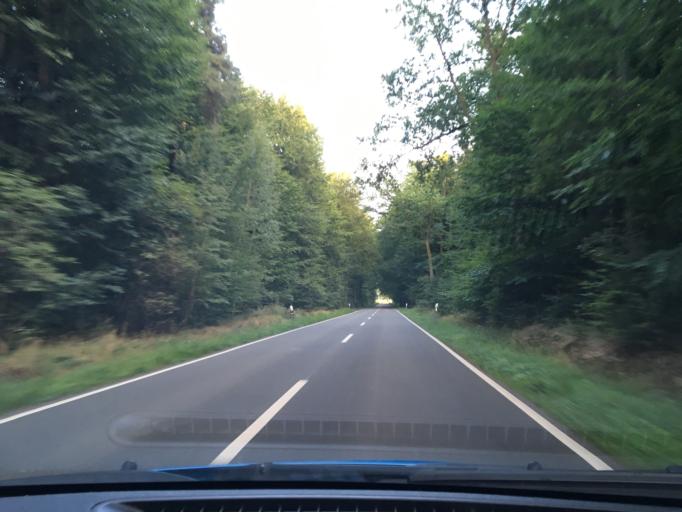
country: DE
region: Lower Saxony
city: Tosterglope
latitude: 53.2258
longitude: 10.8061
